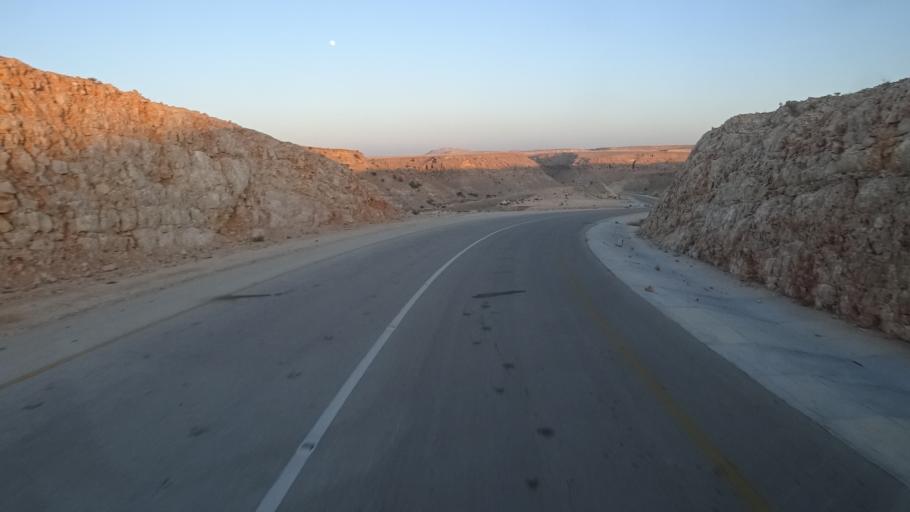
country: YE
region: Al Mahrah
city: Hawf
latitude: 16.9558
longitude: 53.3312
